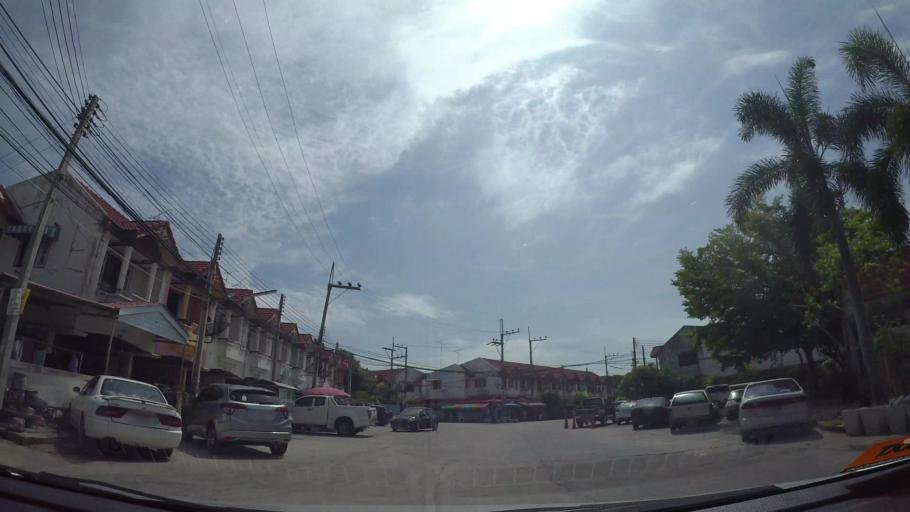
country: TH
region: Chon Buri
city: Chon Buri
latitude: 13.3227
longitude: 100.9474
